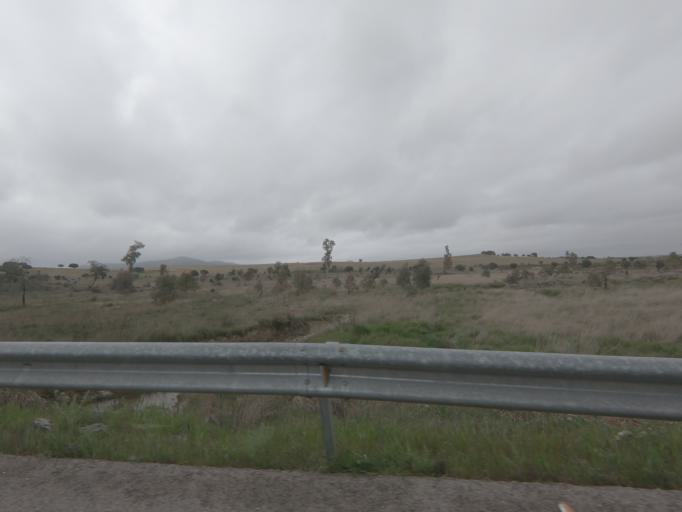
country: ES
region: Extremadura
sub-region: Provincia de Caceres
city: Malpartida de Caceres
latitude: 39.3290
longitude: -6.4899
